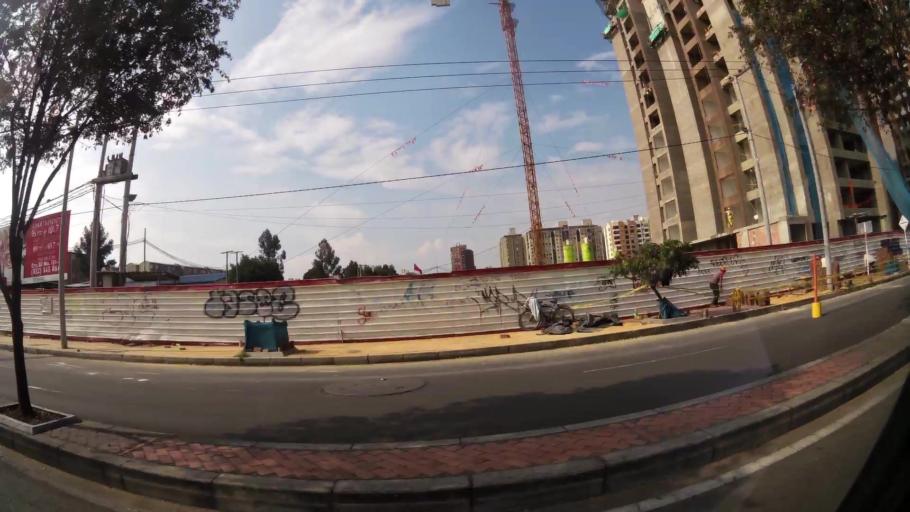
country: CO
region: Cundinamarca
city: Cota
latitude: 4.7386
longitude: -74.0611
